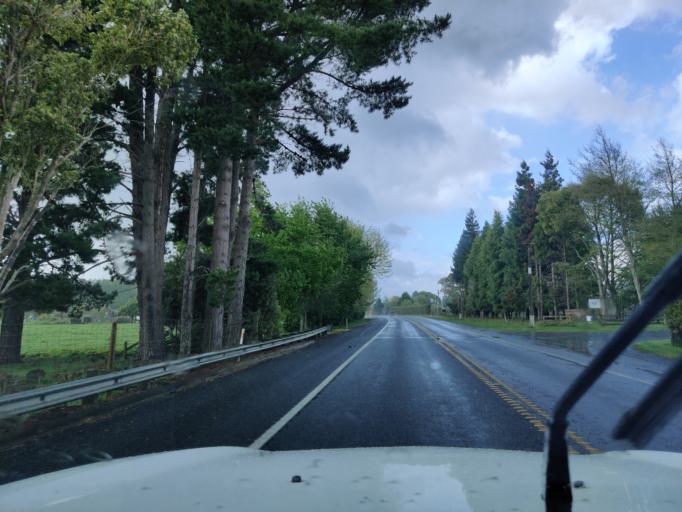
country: NZ
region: Waikato
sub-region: Waipa District
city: Cambridge
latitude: -37.9363
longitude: 175.5751
